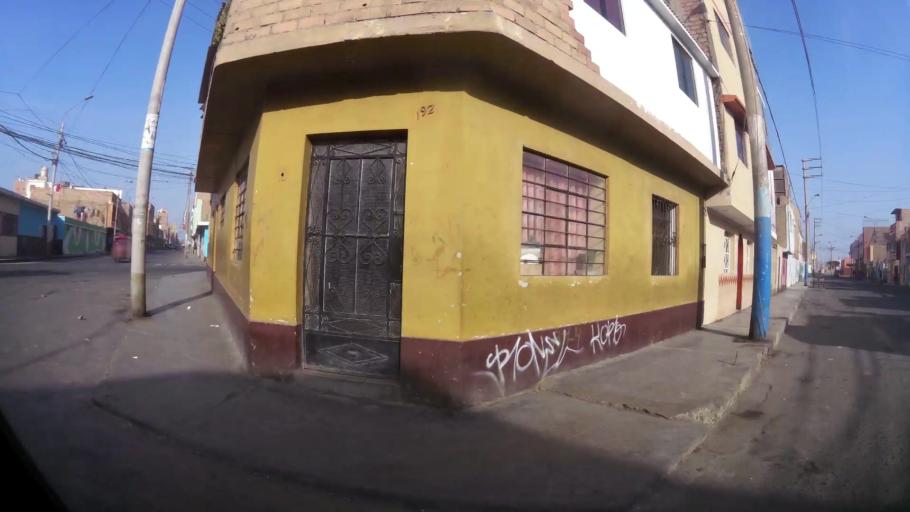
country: PE
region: Lima
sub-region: Huaura
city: Huacho
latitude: -11.1064
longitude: -77.6127
